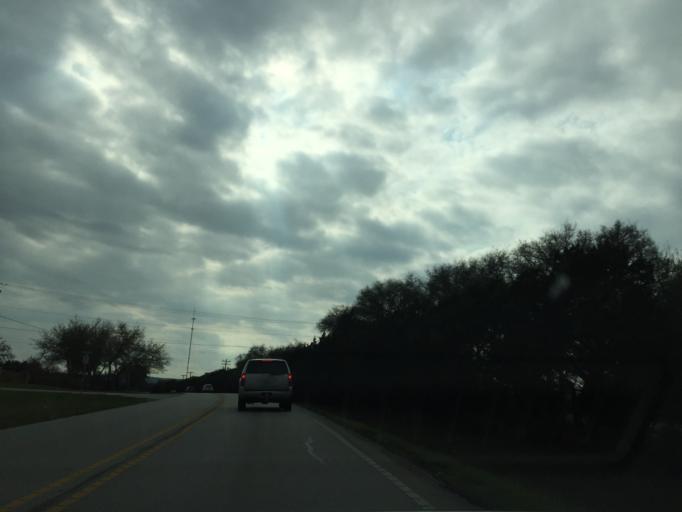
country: US
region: Texas
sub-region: Hays County
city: Dripping Springs
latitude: 30.1398
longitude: -98.0018
